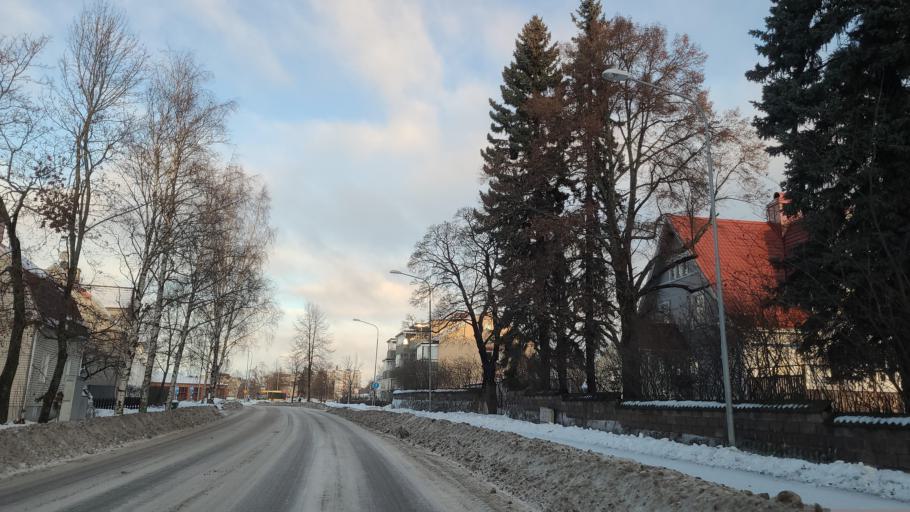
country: SE
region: Gaevleborg
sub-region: Bollnas Kommun
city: Bollnas
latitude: 61.3513
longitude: 16.3997
